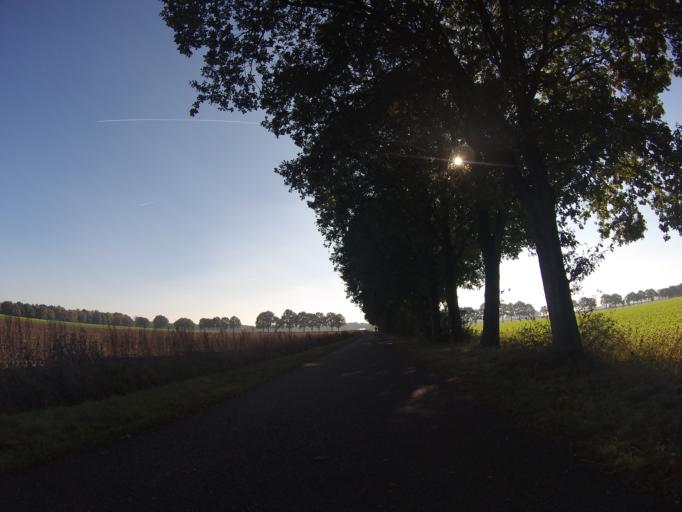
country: NL
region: Drenthe
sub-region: Gemeente Coevorden
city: Dalen
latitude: 52.7690
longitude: 6.7117
